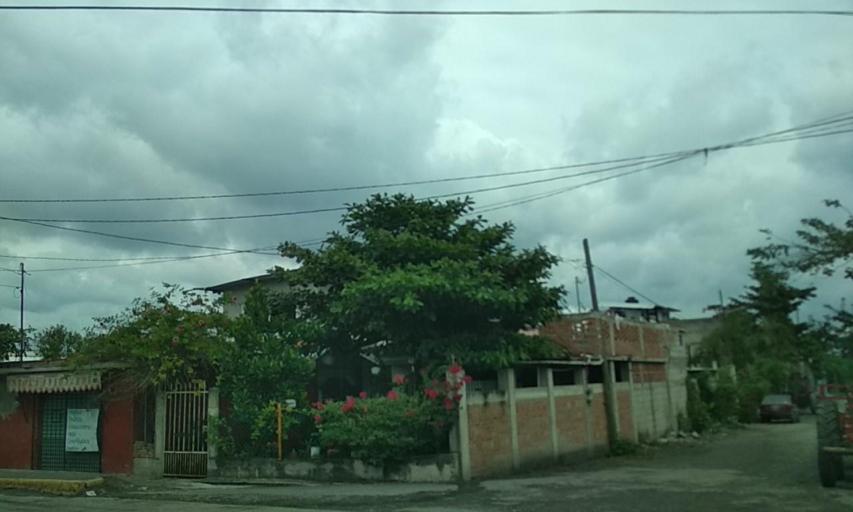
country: MX
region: Veracruz
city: Agua Dulce
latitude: 20.3624
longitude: -97.3311
